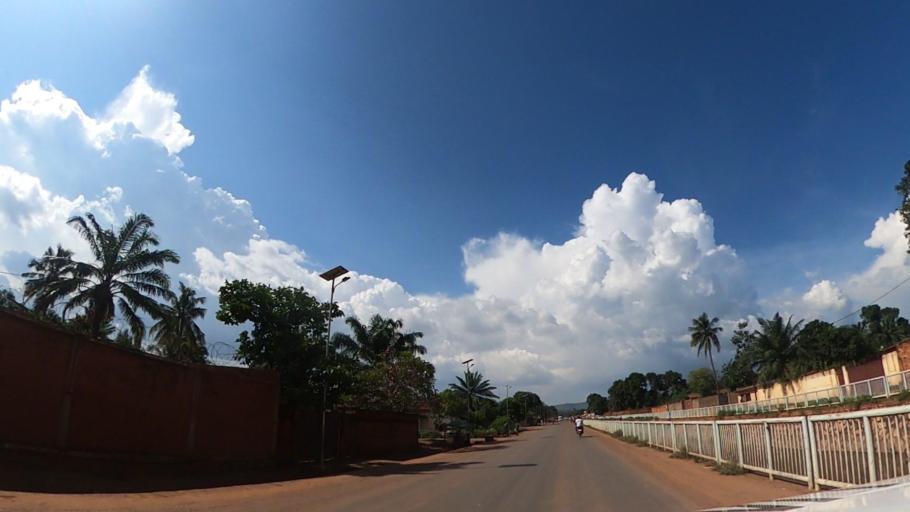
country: CF
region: Bangui
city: Bangui
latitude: 4.3721
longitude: 18.5525
